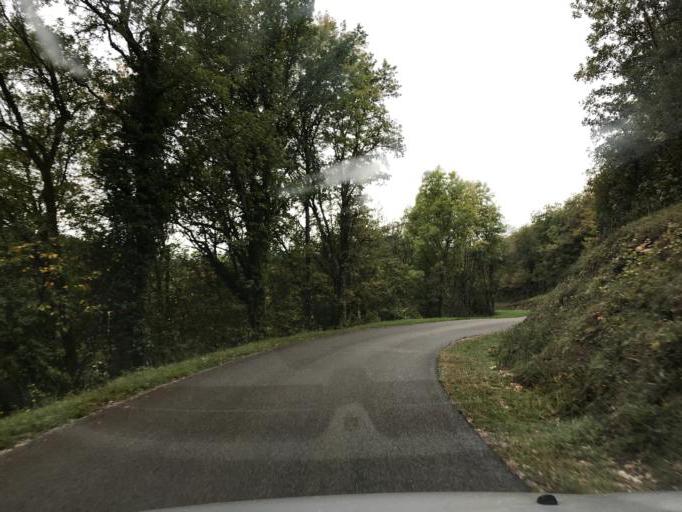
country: FR
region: Franche-Comte
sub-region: Departement du Jura
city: Arinthod
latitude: 46.4451
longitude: 5.5054
